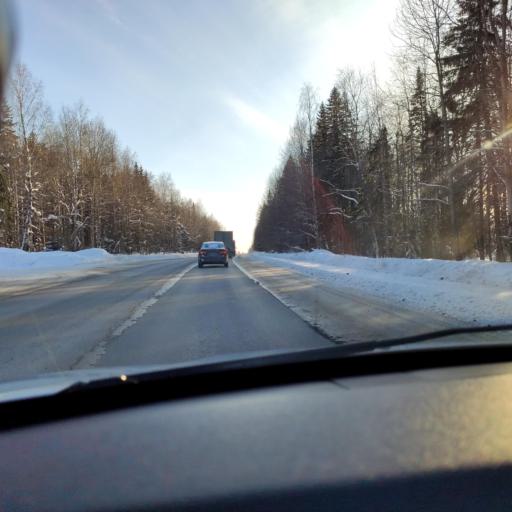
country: RU
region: Perm
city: Dobryanka
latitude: 58.3893
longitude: 56.5010
